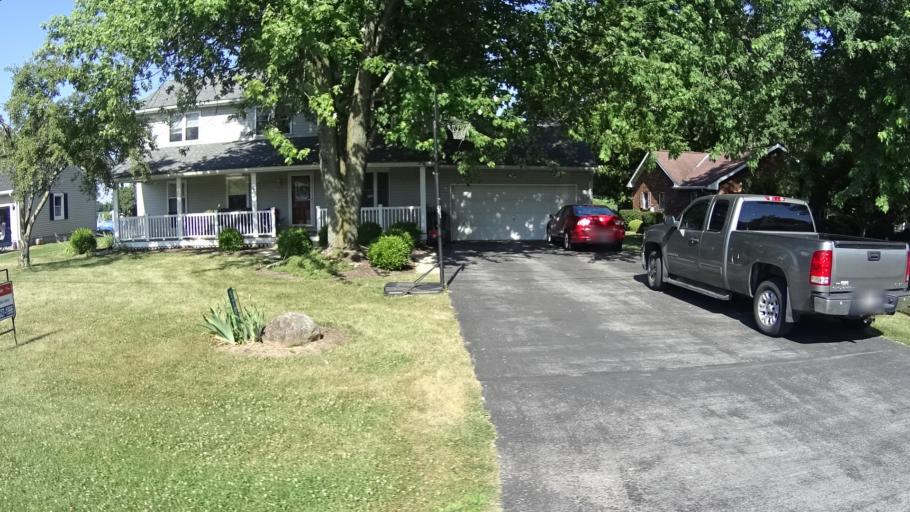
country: US
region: Ohio
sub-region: Huron County
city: Bellevue
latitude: 41.3714
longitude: -82.8021
